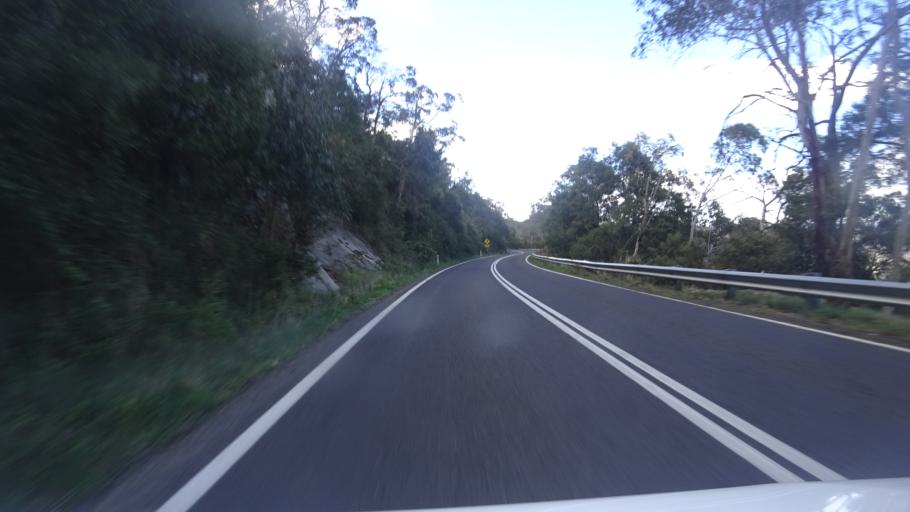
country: AU
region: New South Wales
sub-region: Lithgow
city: Bowenfels
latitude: -33.6630
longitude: 150.0509
